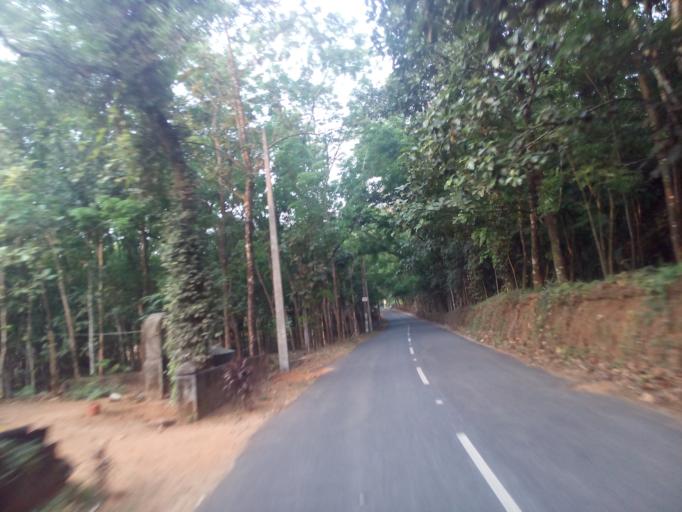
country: IN
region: Kerala
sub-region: Kottayam
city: Palackattumala
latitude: 9.8190
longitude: 76.6673
